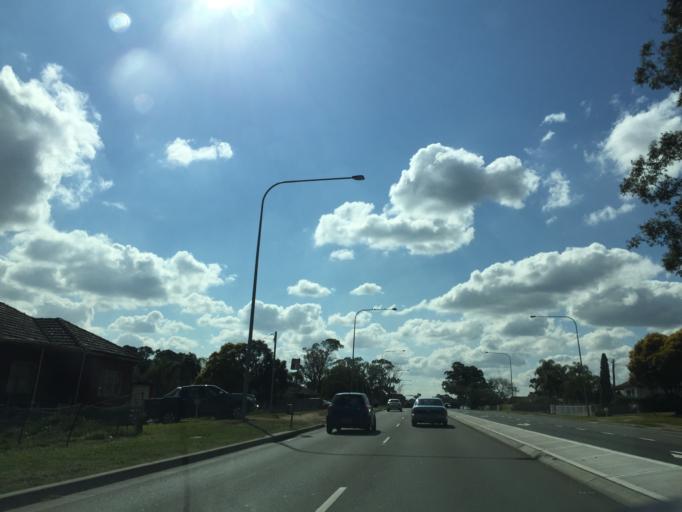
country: AU
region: New South Wales
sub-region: Blacktown
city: Quakers Hill
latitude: -33.7416
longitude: 150.8708
